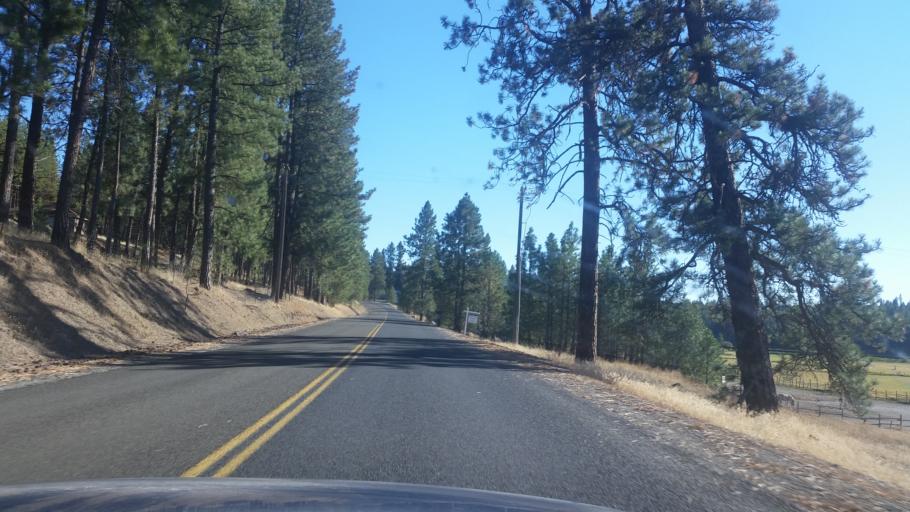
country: US
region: Washington
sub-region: Spokane County
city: Cheney
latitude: 47.5590
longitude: -117.4883
